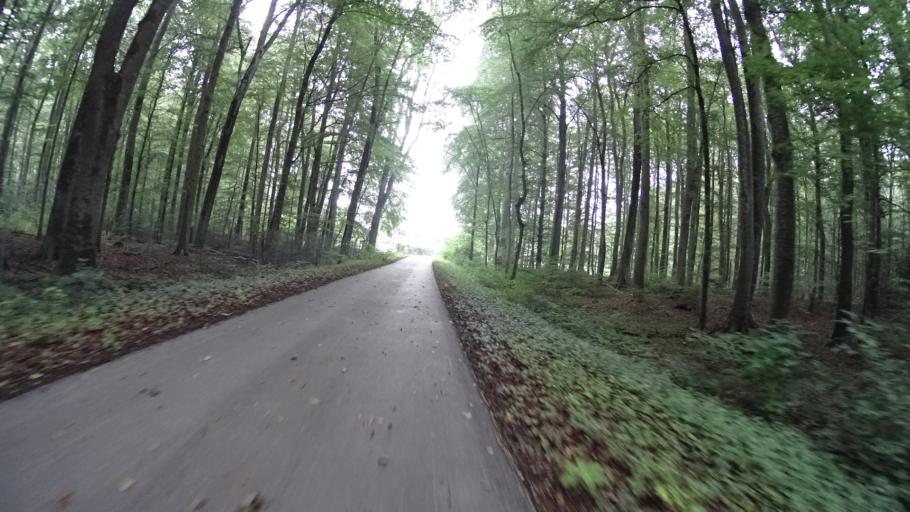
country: DE
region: Bavaria
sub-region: Upper Bavaria
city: Stammham
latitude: 48.8731
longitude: 11.5099
